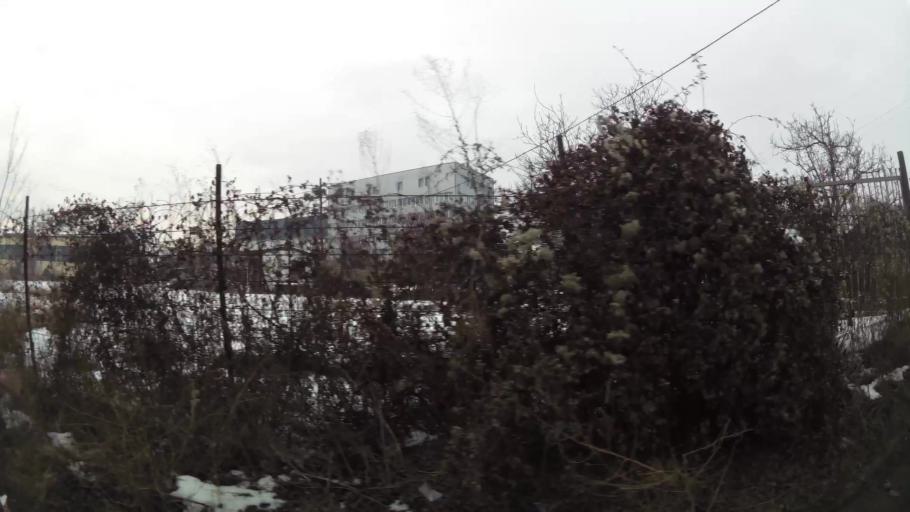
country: MK
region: Suto Orizari
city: Suto Orizare
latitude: 42.0480
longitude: 21.4284
